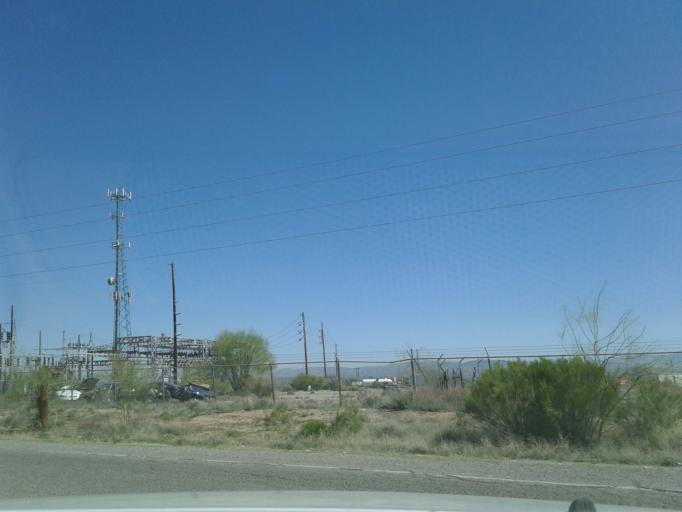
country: US
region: Arizona
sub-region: Pima County
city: Avra Valley
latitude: 32.4450
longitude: -111.3043
